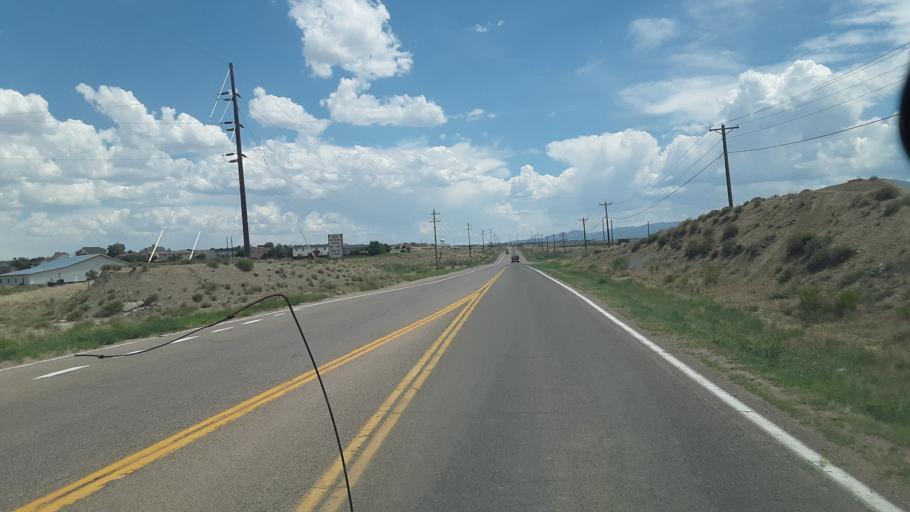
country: US
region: Colorado
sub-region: Fremont County
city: Florence
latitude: 38.3771
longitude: -105.1107
